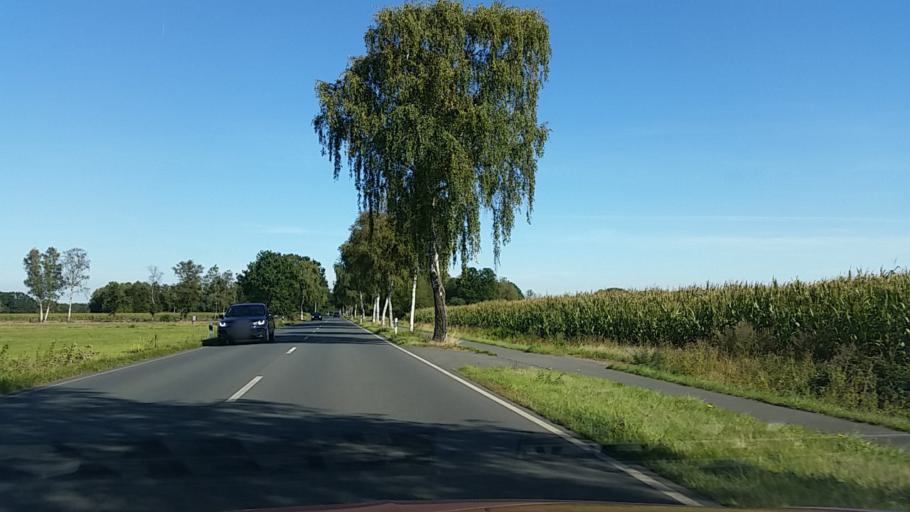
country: DE
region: Lower Saxony
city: Schneverdingen
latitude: 53.1747
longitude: 9.8147
